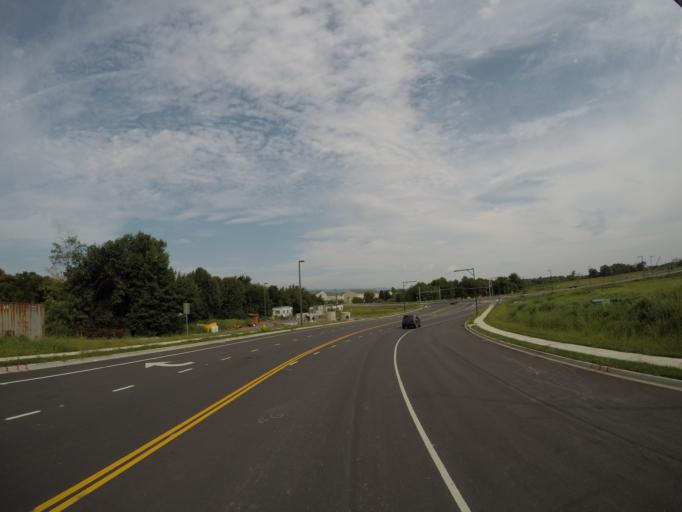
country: US
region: Maryland
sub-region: Frederick County
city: Clover Hill
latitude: 39.4596
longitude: -77.4055
